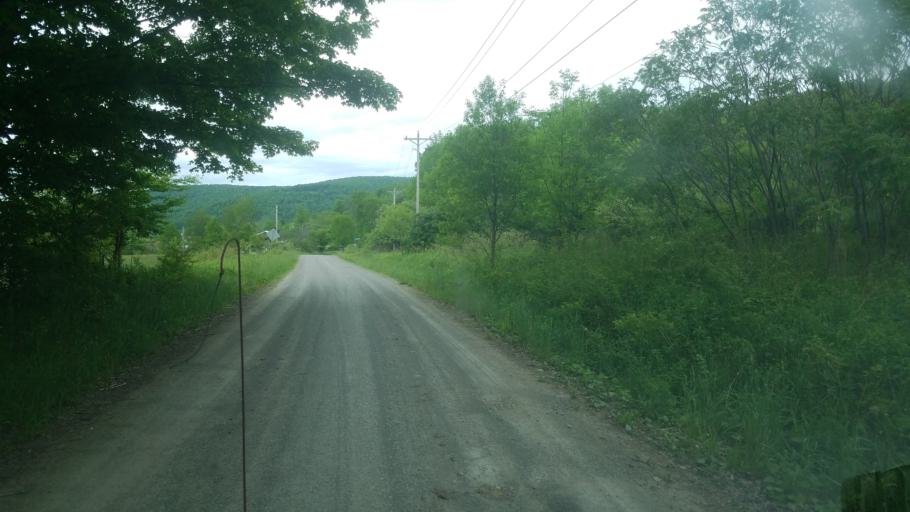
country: US
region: Pennsylvania
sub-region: Tioga County
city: Westfield
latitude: 41.8696
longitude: -77.5968
